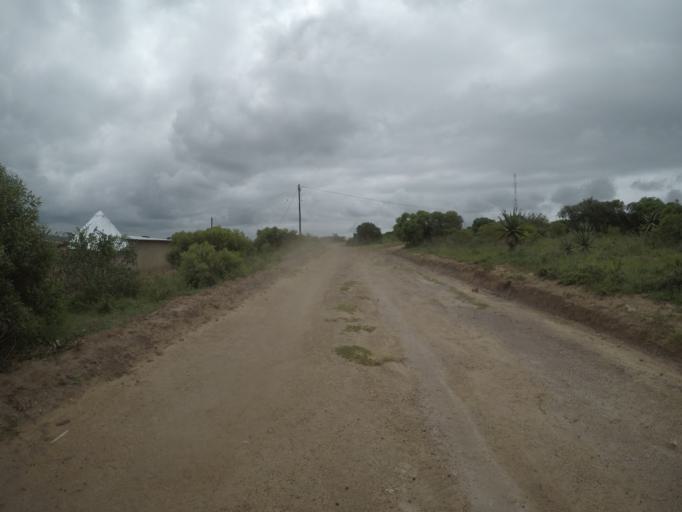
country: ZA
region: KwaZulu-Natal
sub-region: uThungulu District Municipality
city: Empangeni
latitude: -28.6051
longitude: 31.8324
